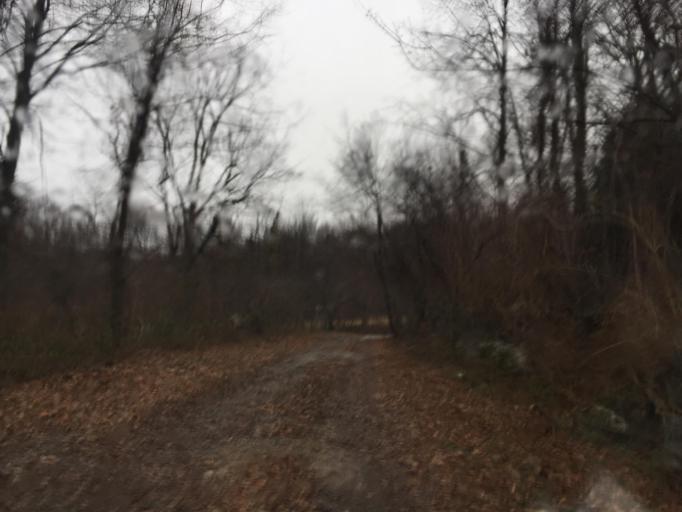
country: SI
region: Kanal
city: Kanal
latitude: 46.0736
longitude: 13.6750
